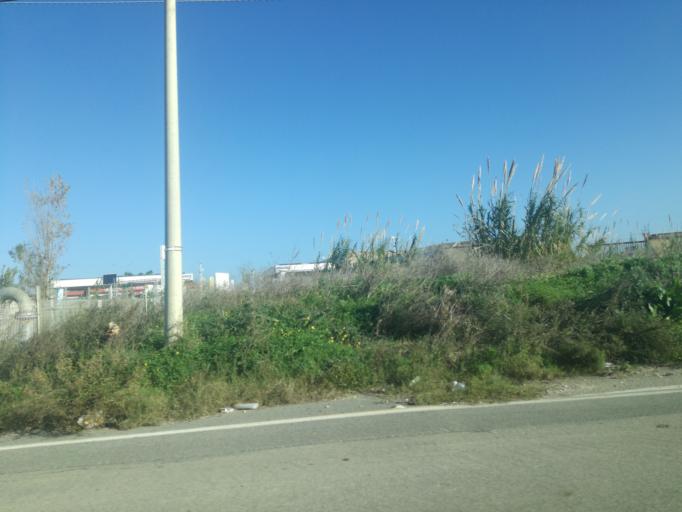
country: IT
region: Sicily
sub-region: Provincia di Caltanissetta
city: Gela
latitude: 37.0616
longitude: 14.2737
